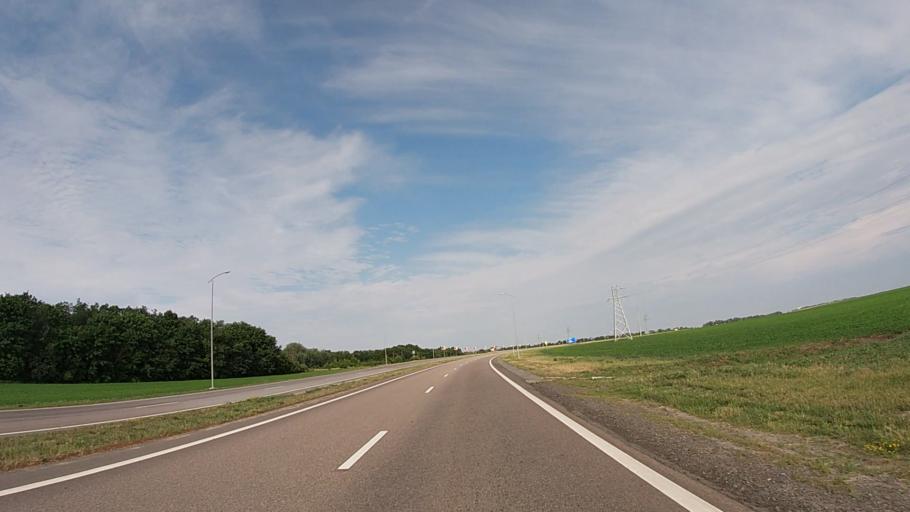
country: RU
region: Belgorod
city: Rakitnoye
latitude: 50.7903
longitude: 35.8732
